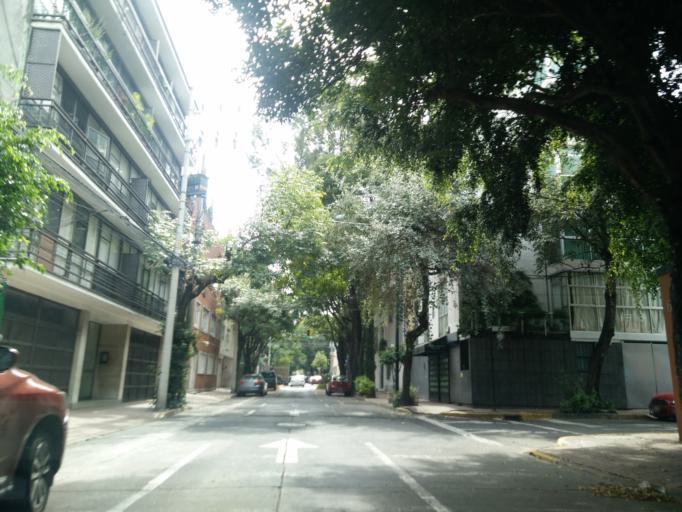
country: MX
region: Mexico City
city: Polanco
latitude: 19.4131
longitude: -99.1849
